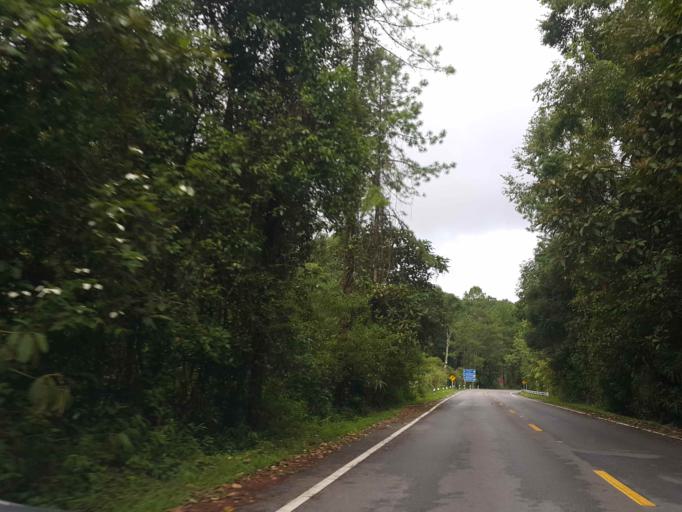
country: TH
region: Chiang Mai
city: Mae Chaem
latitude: 18.5287
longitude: 98.4970
